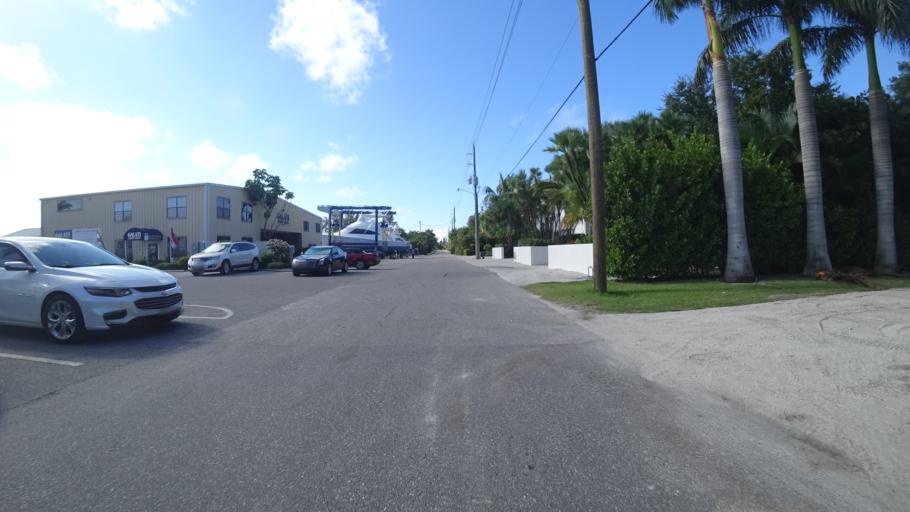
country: US
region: Florida
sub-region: Manatee County
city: Anna Maria
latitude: 27.5274
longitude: -82.7211
